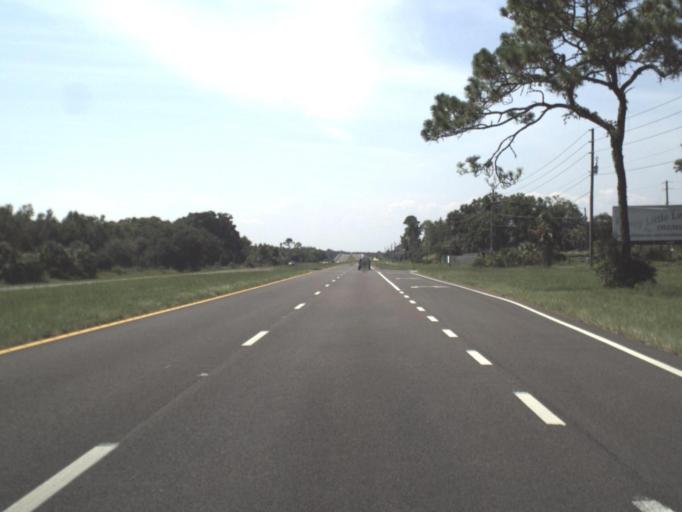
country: US
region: Florida
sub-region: Levy County
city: Inglis
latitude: 29.0021
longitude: -82.6562
